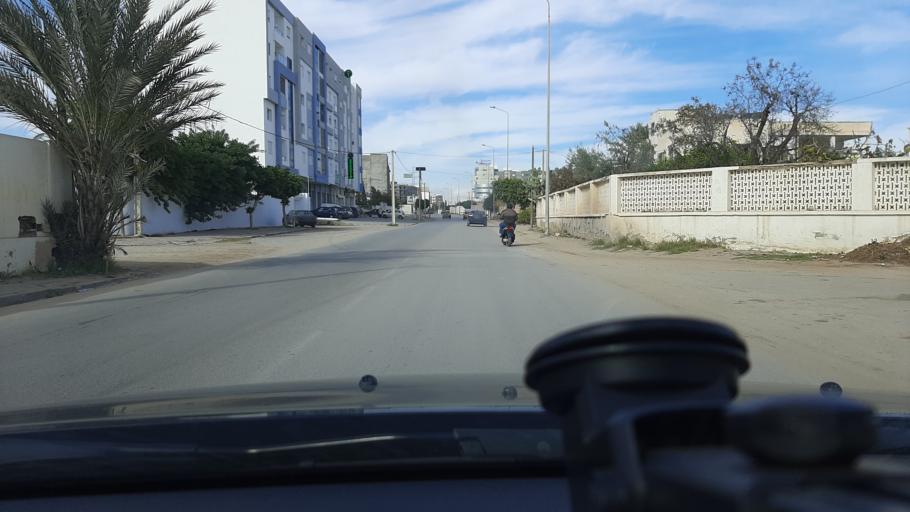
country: TN
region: Safaqis
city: Sfax
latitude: 34.7594
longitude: 10.7324
